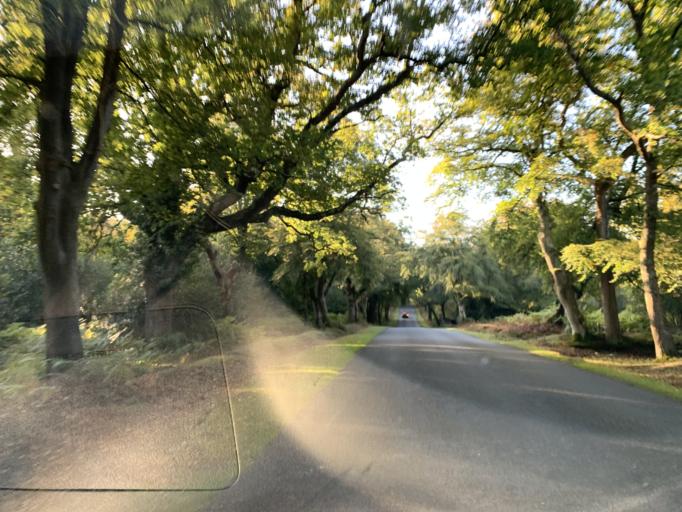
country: GB
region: England
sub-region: Hampshire
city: West Wellow
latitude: 50.9527
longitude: -1.6288
